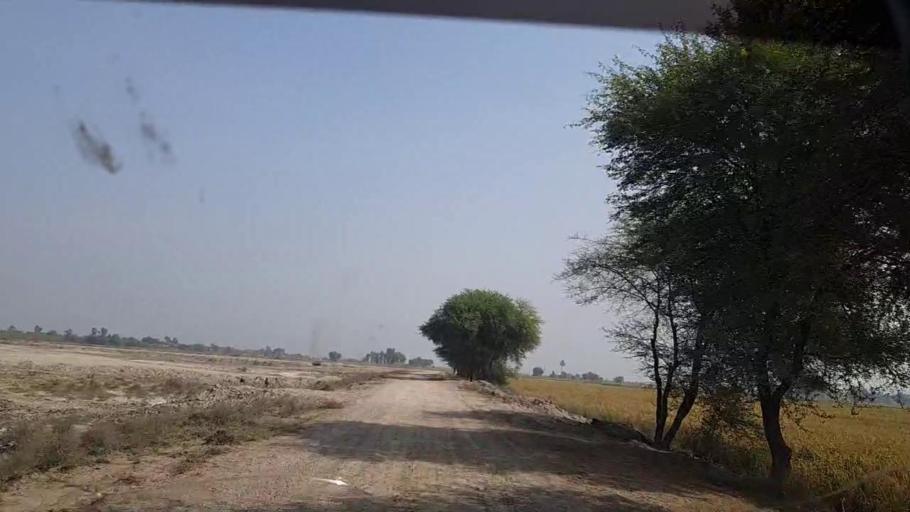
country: PK
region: Sindh
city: Shikarpur
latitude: 28.0513
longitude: 68.6672
